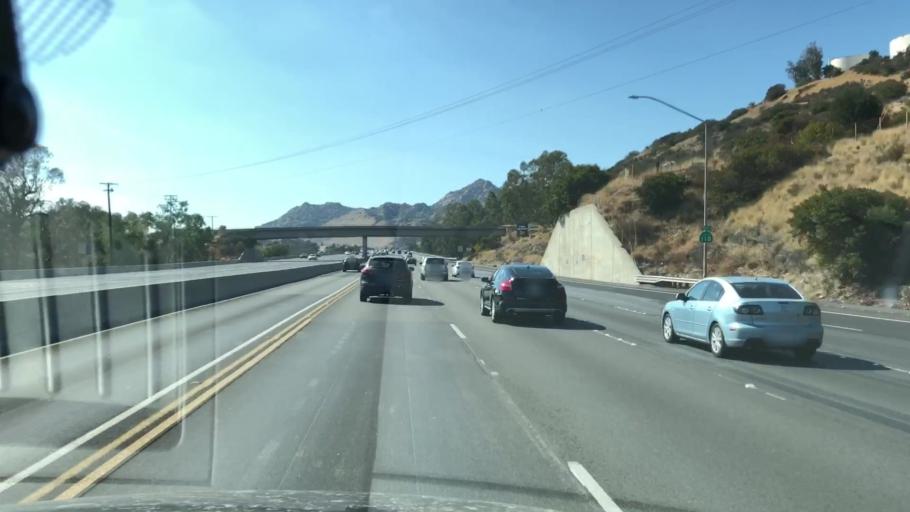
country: US
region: California
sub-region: Los Angeles County
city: Chatsworth
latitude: 34.2781
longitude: -118.6086
